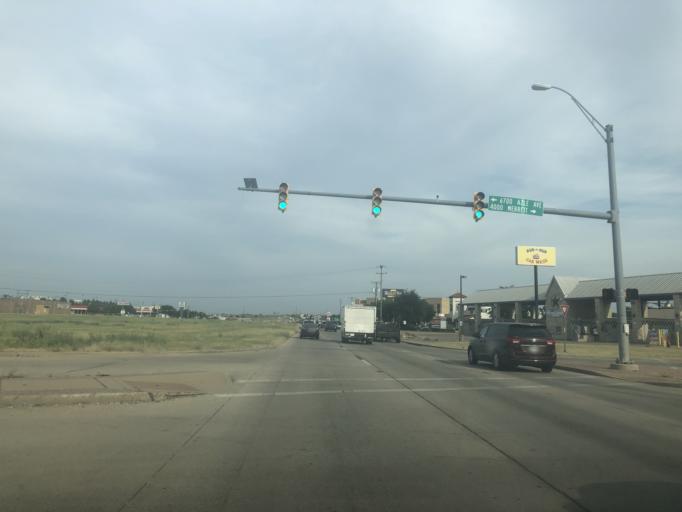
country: US
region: Texas
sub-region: Tarrant County
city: Lake Worth
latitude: 32.8141
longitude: -97.4376
